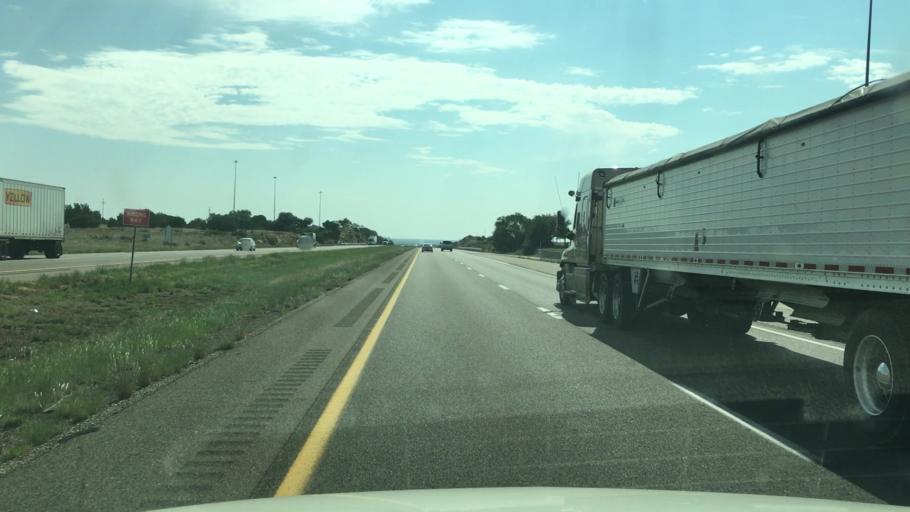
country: US
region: New Mexico
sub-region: Guadalupe County
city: Santa Rosa
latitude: 34.9812
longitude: -105.0865
